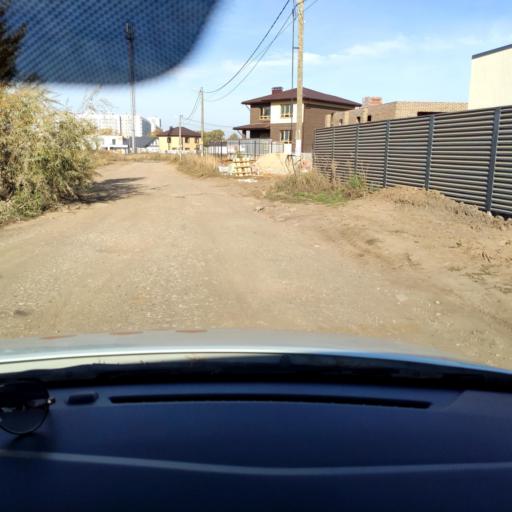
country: RU
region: Tatarstan
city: Vysokaya Gora
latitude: 55.7885
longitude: 49.2597
